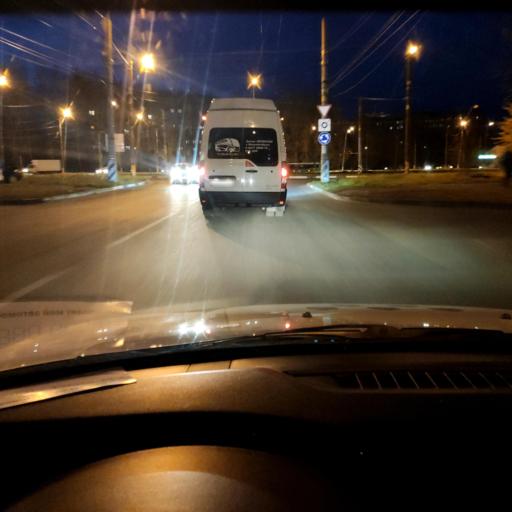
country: RU
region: Samara
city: Tol'yatti
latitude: 53.5132
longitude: 49.4541
